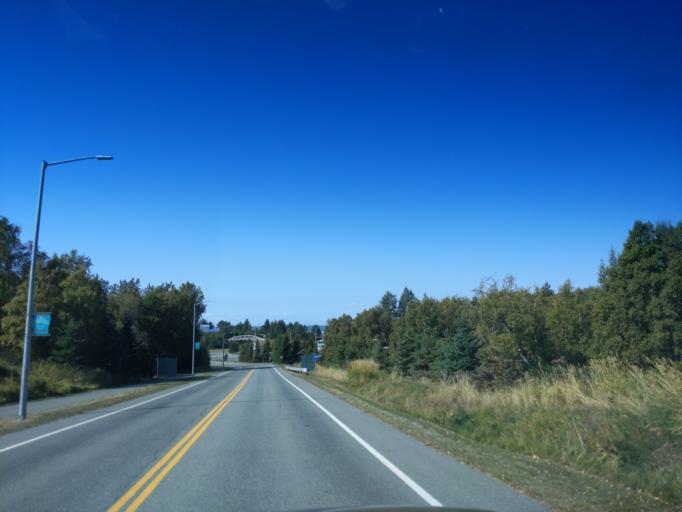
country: US
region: Alaska
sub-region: Anchorage Municipality
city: Anchorage
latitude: 61.1545
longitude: -150.0446
